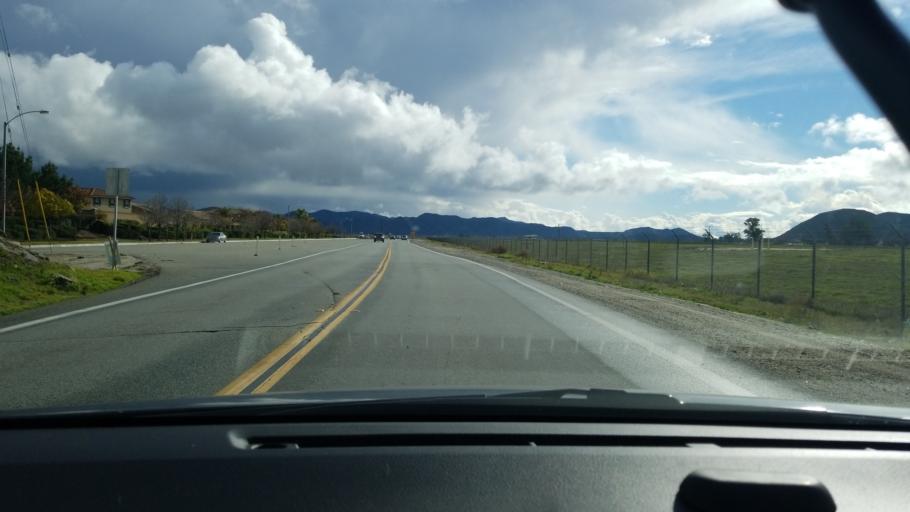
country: US
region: California
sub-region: Riverside County
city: Green Acres
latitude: 33.7550
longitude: -117.0363
